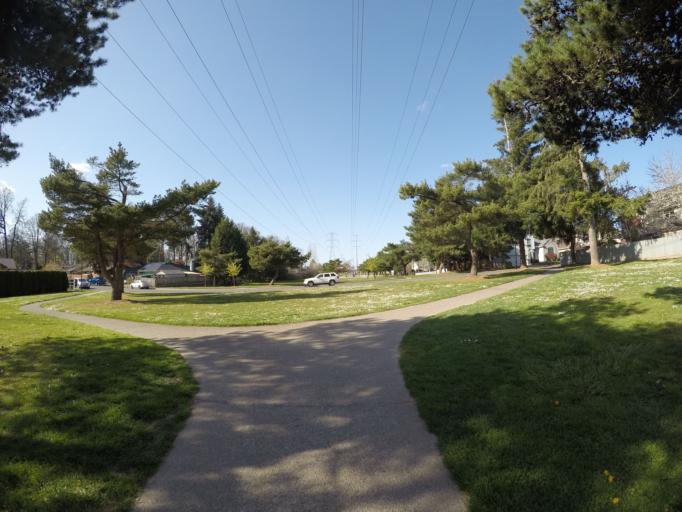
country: US
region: Oregon
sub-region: Washington County
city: Oak Hills
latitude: 45.5451
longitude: -122.8465
